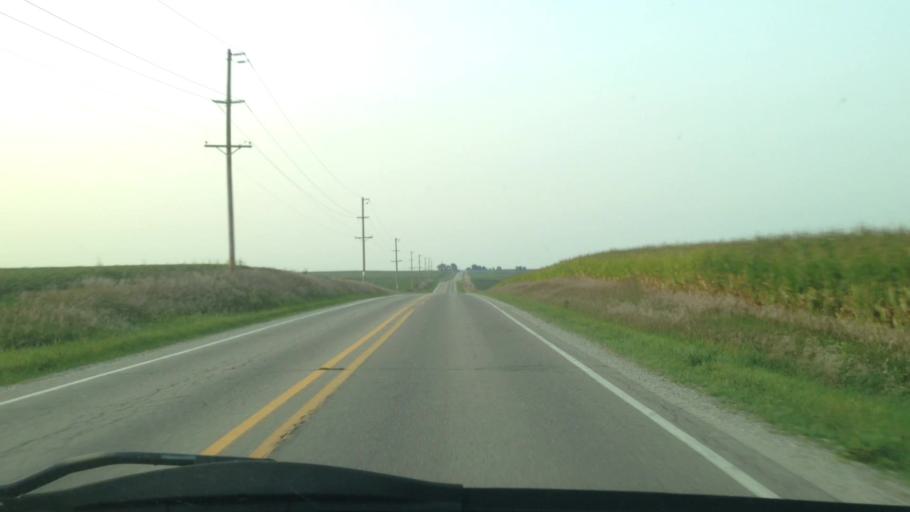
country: US
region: Iowa
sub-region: Iowa County
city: Marengo
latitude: 41.9435
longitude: -92.0850
